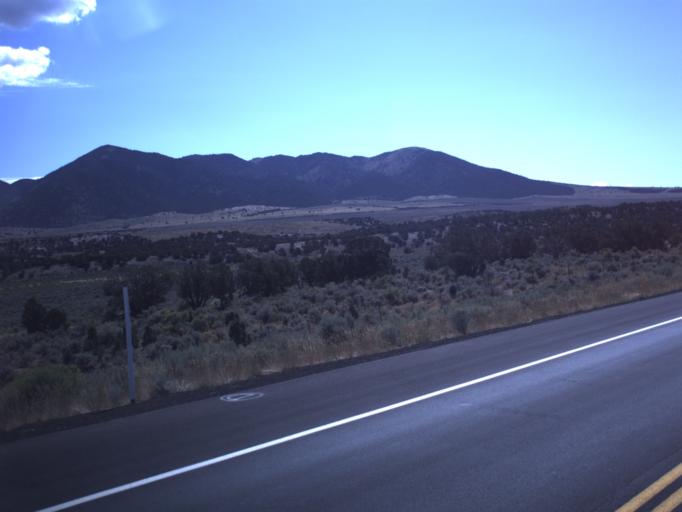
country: US
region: Utah
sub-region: Utah County
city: Eagle Mountain
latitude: 40.0303
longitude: -112.2838
